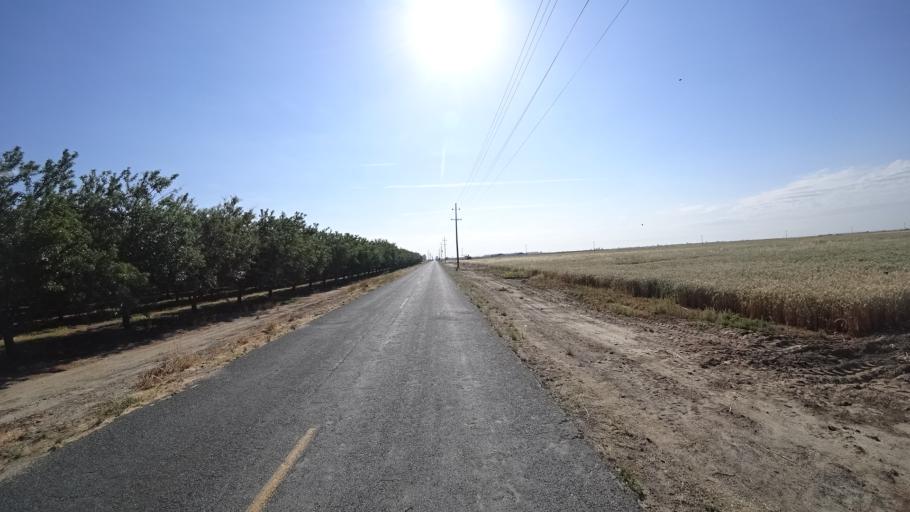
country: US
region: California
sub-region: Kings County
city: Armona
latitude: 36.2256
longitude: -119.7034
